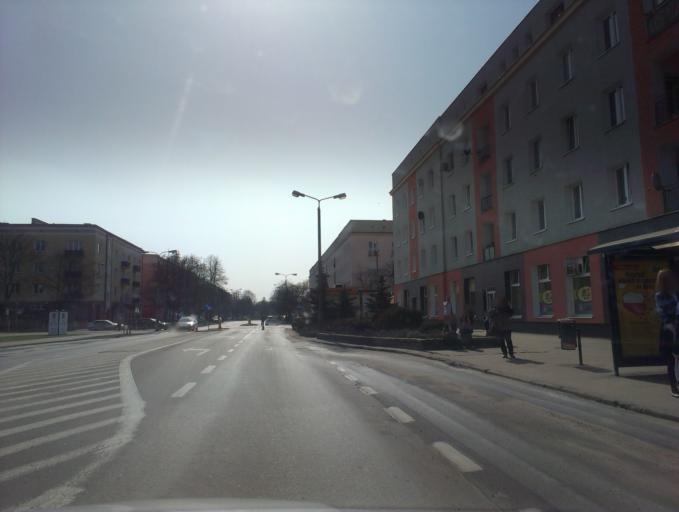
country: PL
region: Kujawsko-Pomorskie
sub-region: Bydgoszcz
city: Bydgoszcz
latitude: 53.1402
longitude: 18.0286
